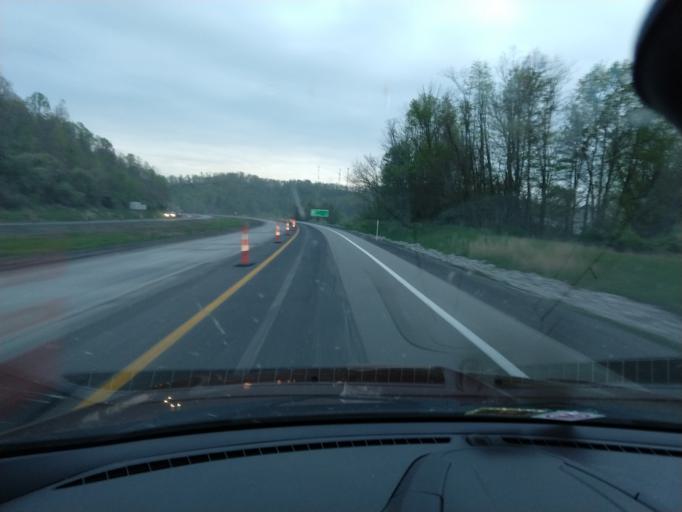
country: US
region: West Virginia
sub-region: Braxton County
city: Sutton
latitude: 38.7172
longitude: -80.6601
